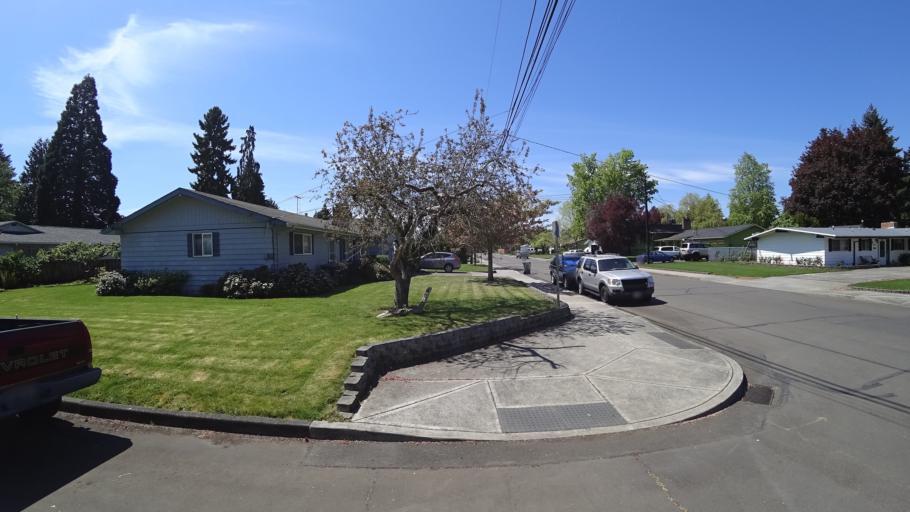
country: US
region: Oregon
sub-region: Washington County
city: Hillsboro
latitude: 45.5114
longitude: -122.9665
